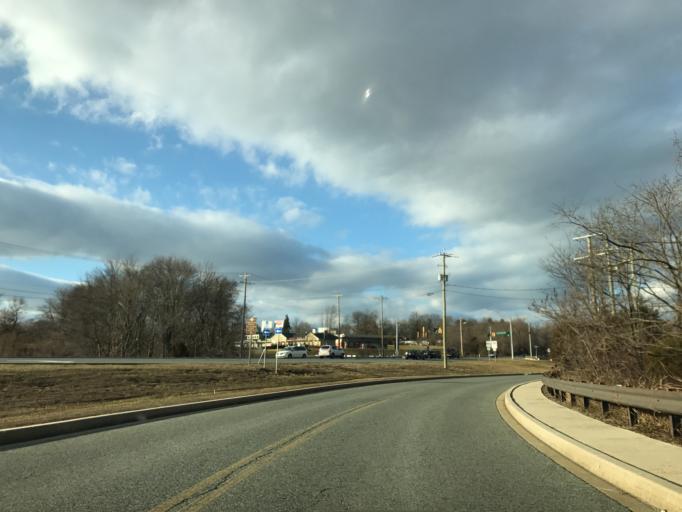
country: US
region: Maryland
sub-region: Cecil County
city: North East
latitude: 39.6395
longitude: -75.9579
